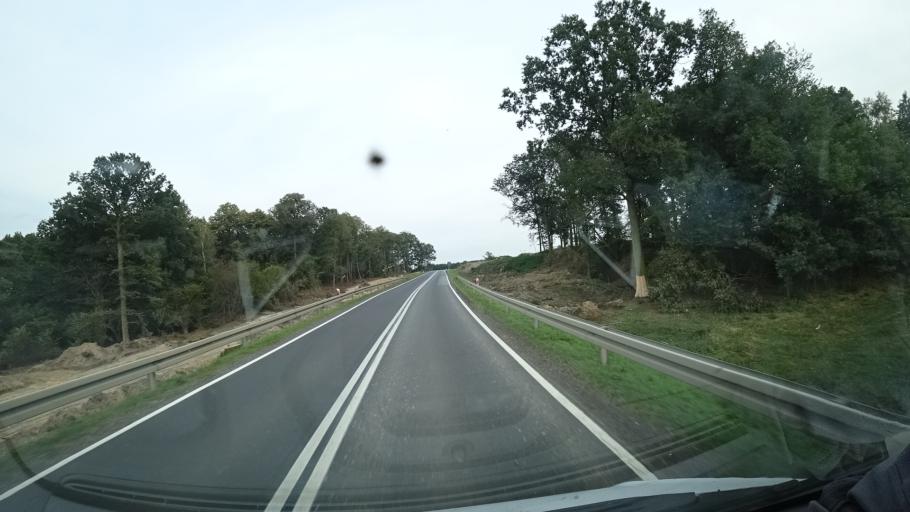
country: PL
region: Silesian Voivodeship
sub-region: Powiat gliwicki
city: Rudziniec
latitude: 50.3887
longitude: 18.3937
